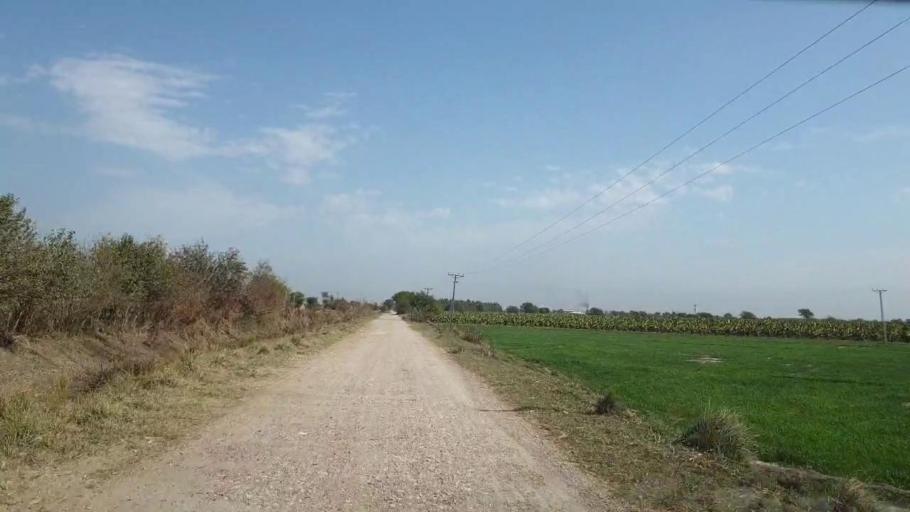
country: PK
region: Sindh
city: Matiari
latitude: 25.5632
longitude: 68.4745
